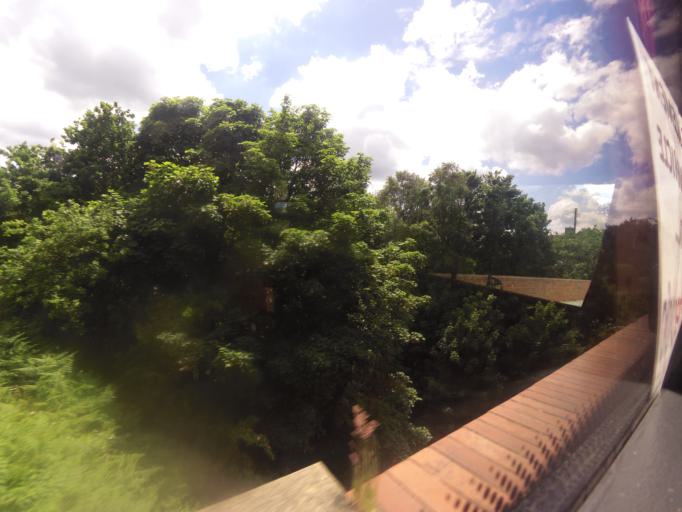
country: GB
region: England
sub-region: Norfolk
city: Cromer
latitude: 52.9226
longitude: 1.2791
